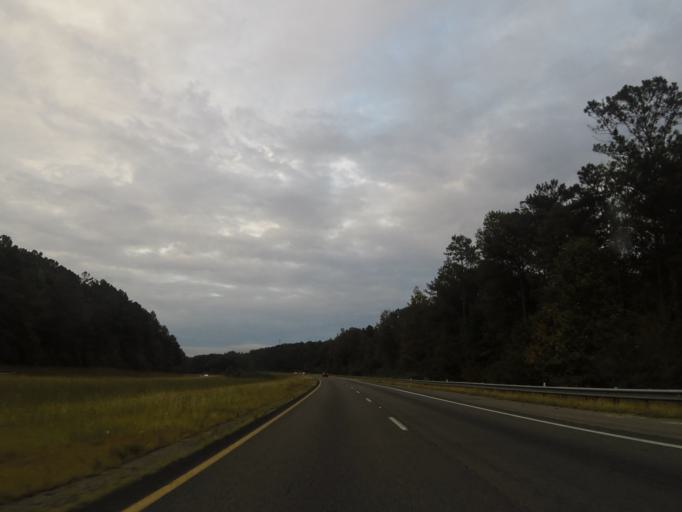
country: US
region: Alabama
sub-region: Saint Clair County
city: Margaret
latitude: 33.7279
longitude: -86.4992
